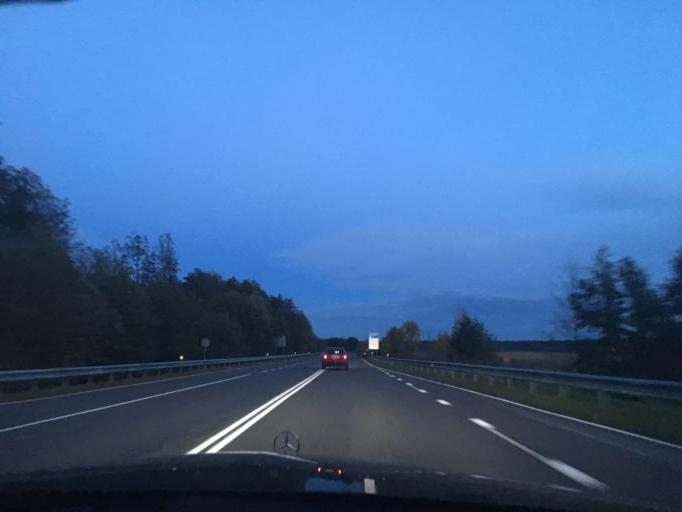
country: PL
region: Lublin Voivodeship
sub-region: Powiat bialski
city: Slawatycze
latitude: 51.7605
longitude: 23.6111
